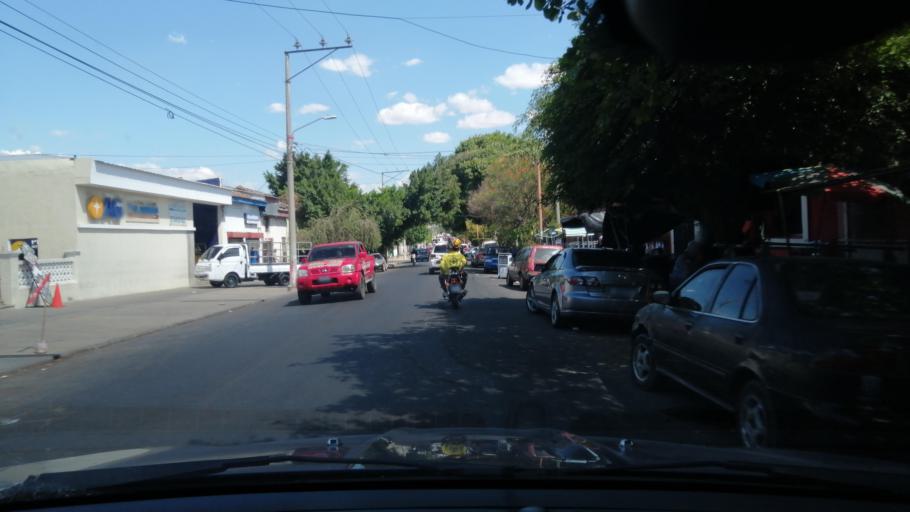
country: SV
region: Santa Ana
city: Santa Ana
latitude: 13.9895
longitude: -89.5613
